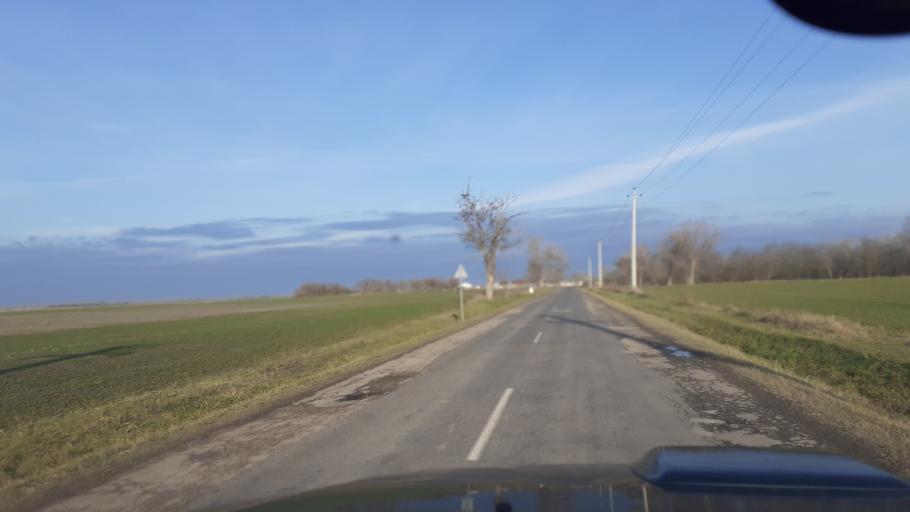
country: HU
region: Pest
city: Domsod
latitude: 47.1061
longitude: 19.0524
